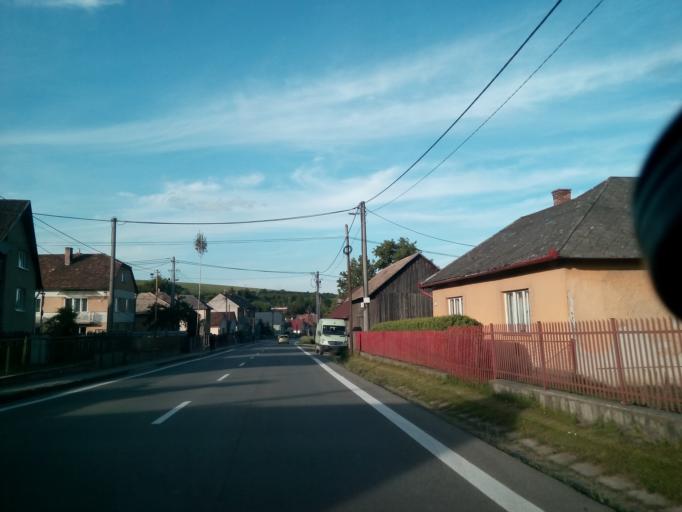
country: SK
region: Kosicky
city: Krompachy
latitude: 49.0149
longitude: 20.9599
